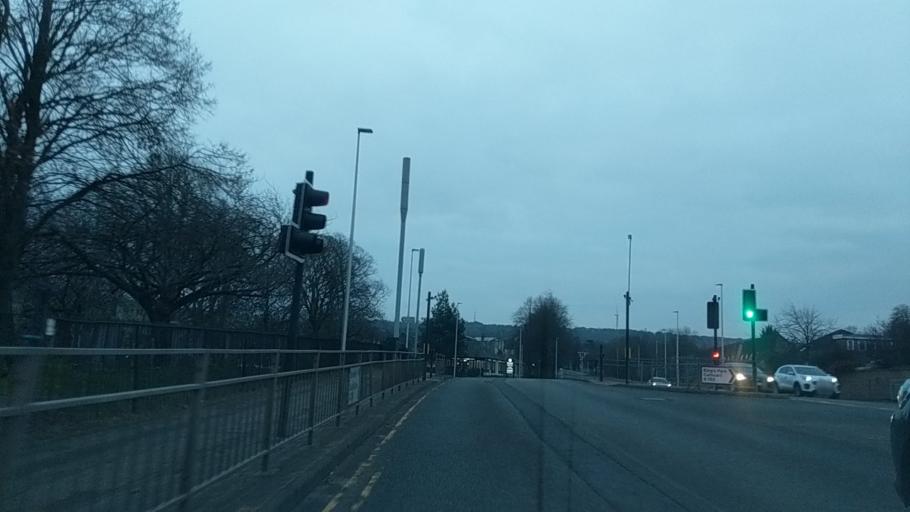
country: GB
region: Scotland
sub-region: South Lanarkshire
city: Rutherglen
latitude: 55.8195
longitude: -4.2152
